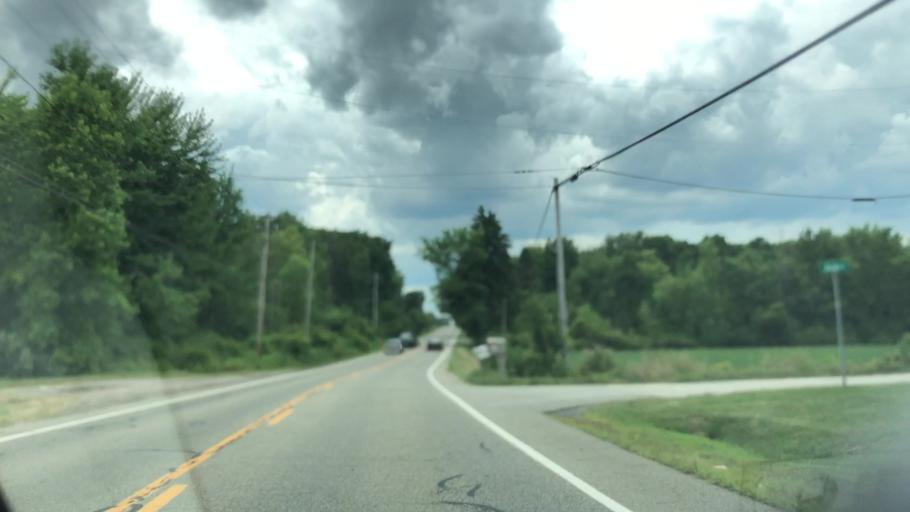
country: US
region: Ohio
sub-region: Summit County
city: Greensburg
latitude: 40.9301
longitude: -81.4478
